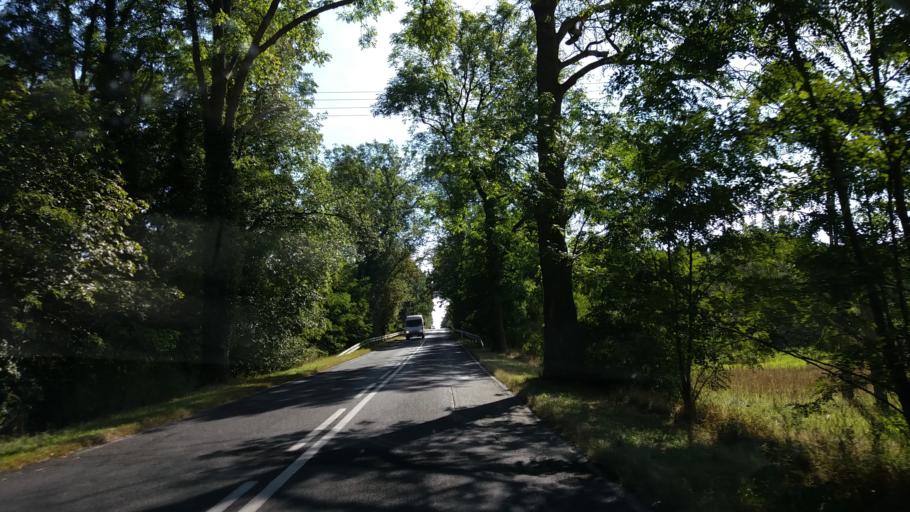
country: PL
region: Lubusz
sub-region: Powiat strzelecko-drezdenecki
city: Drezdenko
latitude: 52.7871
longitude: 15.8384
